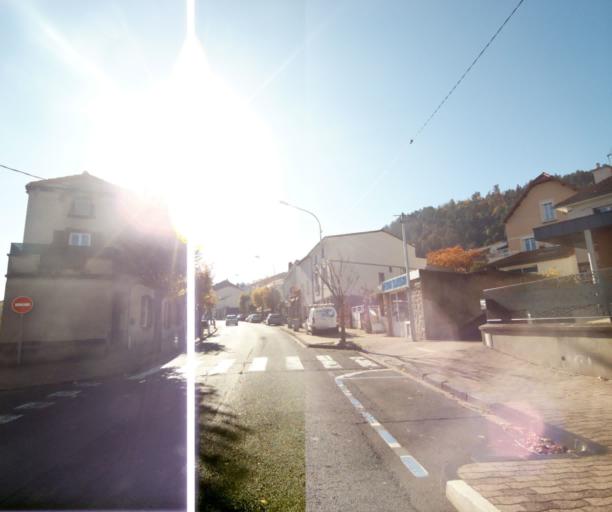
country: FR
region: Auvergne
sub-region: Departement du Puy-de-Dome
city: Ceyrat
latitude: 45.7323
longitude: 3.0637
